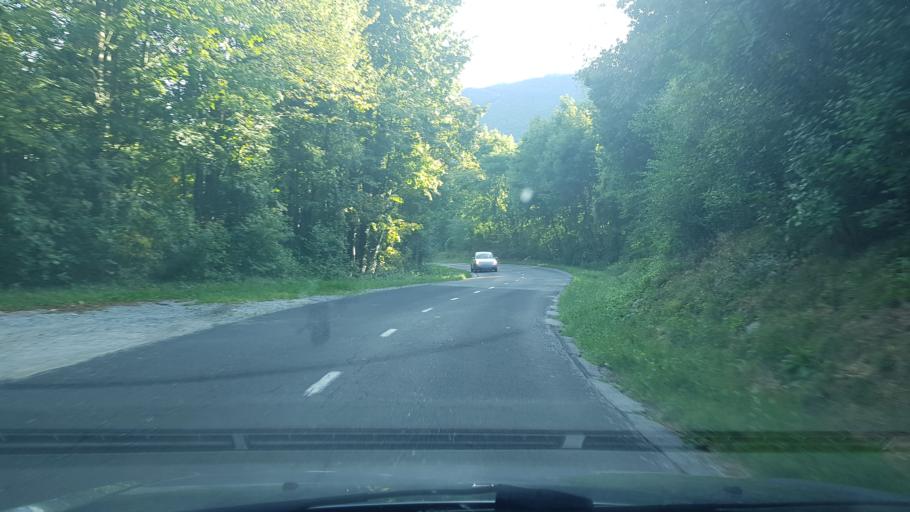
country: SI
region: Nova Gorica
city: Solkan
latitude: 46.0098
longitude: 13.6752
